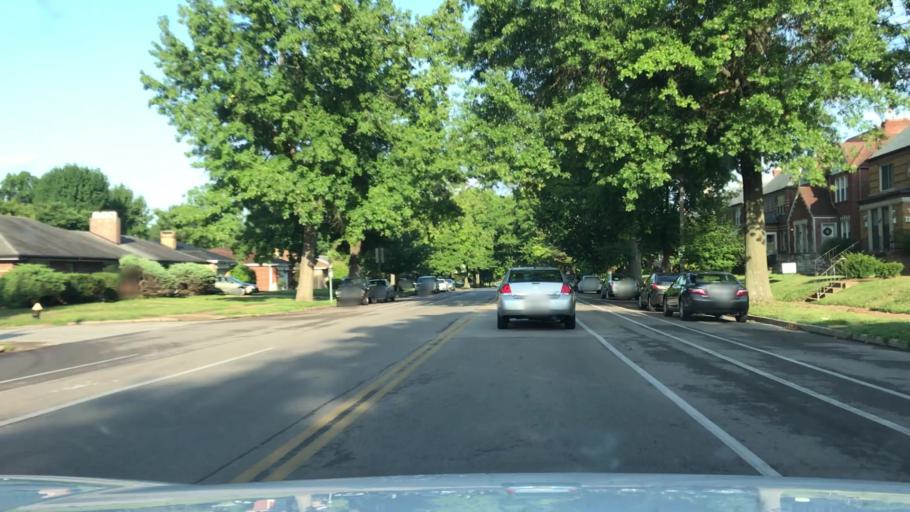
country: US
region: Missouri
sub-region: Saint Louis County
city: Shrewsbury
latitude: 38.5818
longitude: -90.2971
